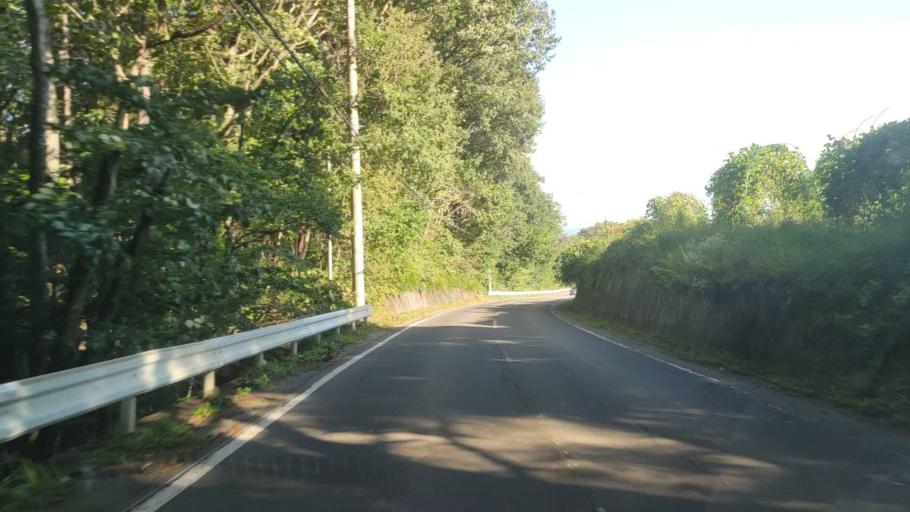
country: JP
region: Nagano
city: Suzaka
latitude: 36.5634
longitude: 138.5557
